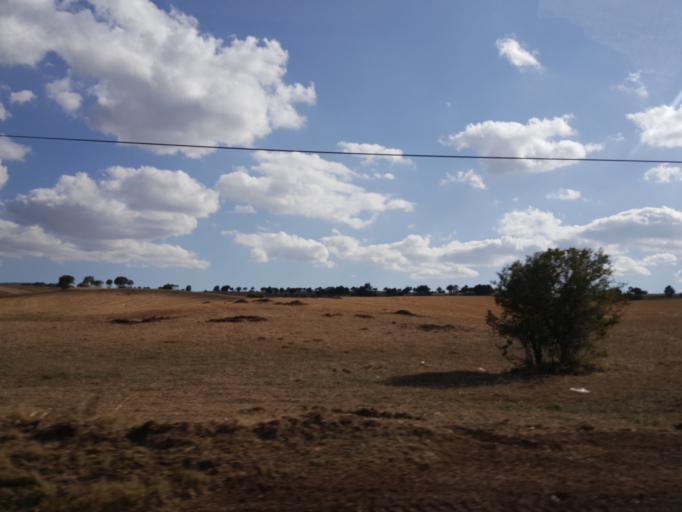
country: TR
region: Tokat
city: Sulusaray
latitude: 40.0016
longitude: 36.1303
